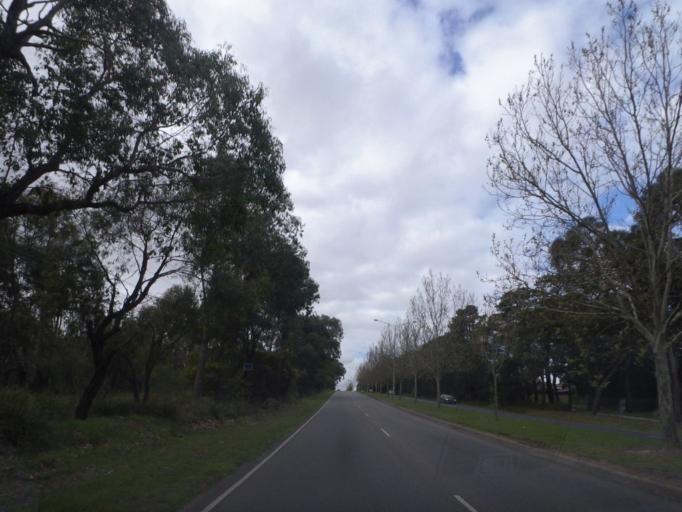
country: AU
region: Victoria
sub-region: Knox
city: Wantirna
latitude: -37.8540
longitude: 145.2192
